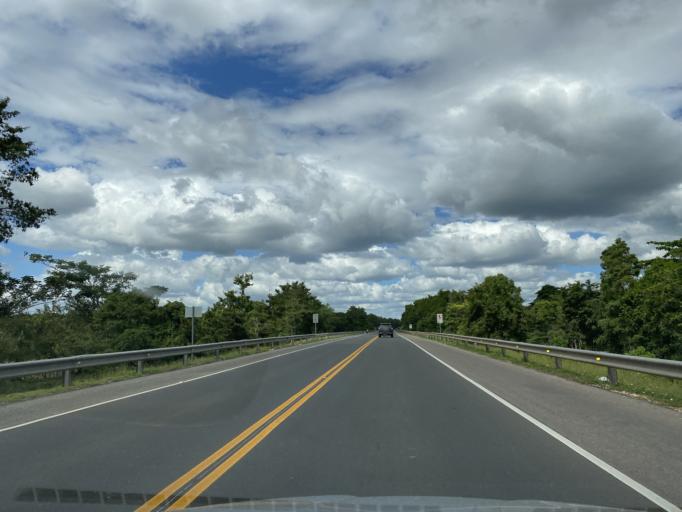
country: DO
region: Santo Domingo
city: Guerra
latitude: 18.5897
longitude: -69.7699
